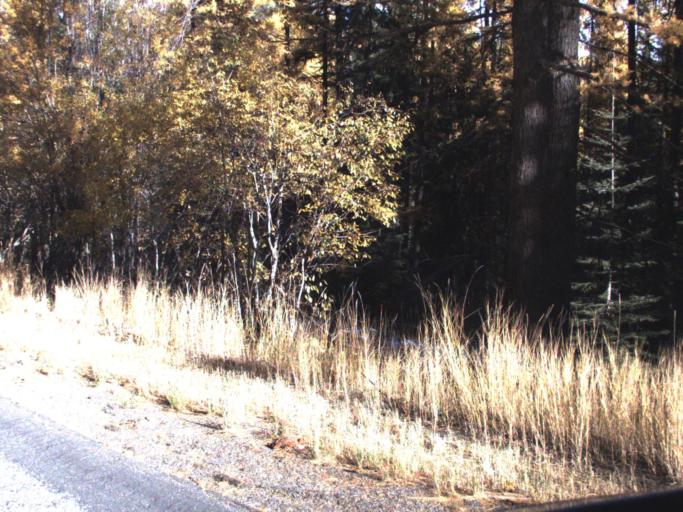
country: US
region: Washington
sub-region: Ferry County
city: Republic
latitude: 48.6151
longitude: -118.4445
